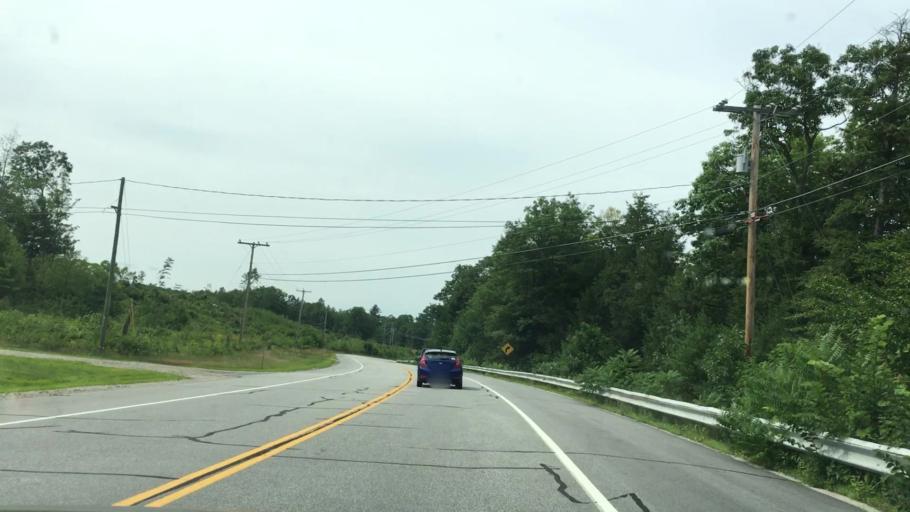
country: US
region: New Hampshire
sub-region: Hillsborough County
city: Hillsborough
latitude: 43.1073
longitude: -71.9171
